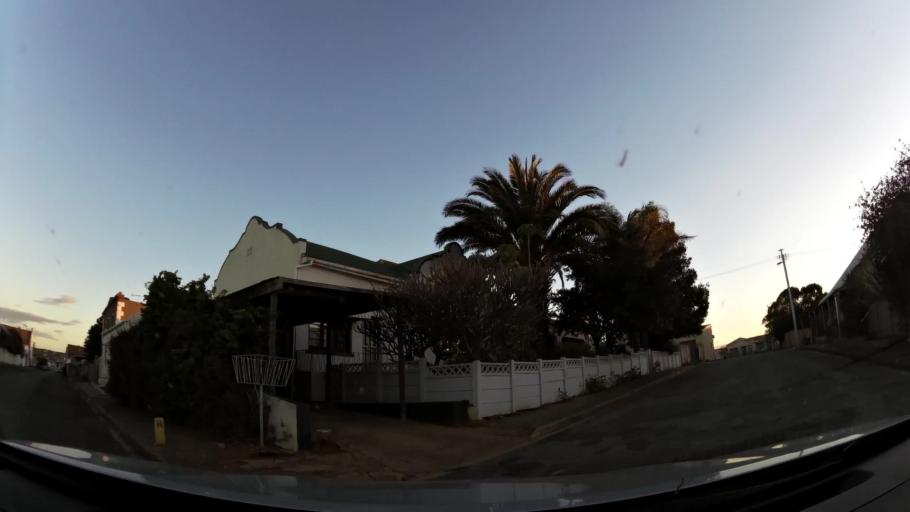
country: ZA
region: Western Cape
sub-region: Eden District Municipality
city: Riversdale
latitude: -34.0884
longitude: 21.2612
